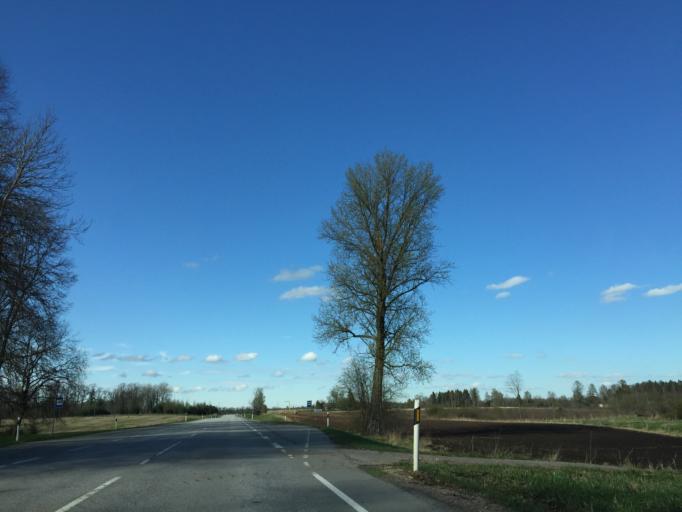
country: EE
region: Vorumaa
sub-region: Antsla vald
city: Vana-Antsla
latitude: 57.8918
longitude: 26.2885
